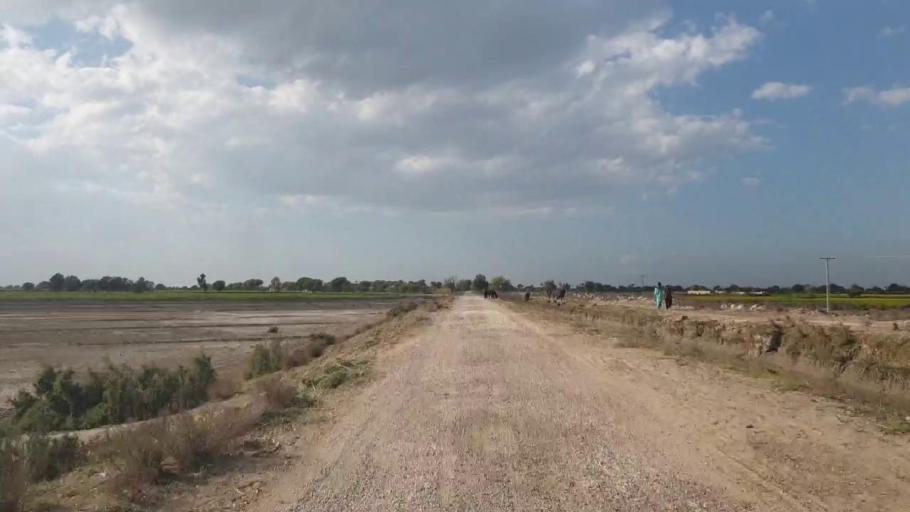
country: PK
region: Sindh
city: Shahdadpur
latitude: 26.0338
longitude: 68.4823
